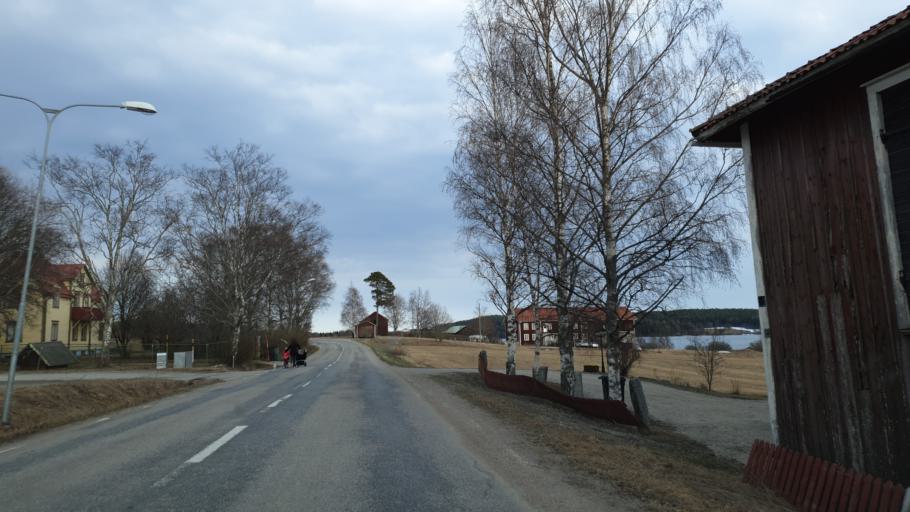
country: SE
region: Gaevleborg
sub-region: Nordanstigs Kommun
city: Bergsjoe
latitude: 61.9737
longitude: 17.2558
